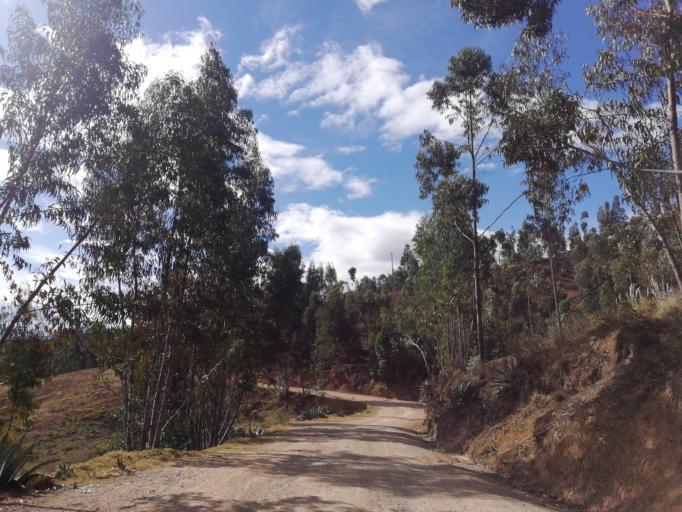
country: CO
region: Boyaca
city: Gameza
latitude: 5.8062
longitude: -72.8083
